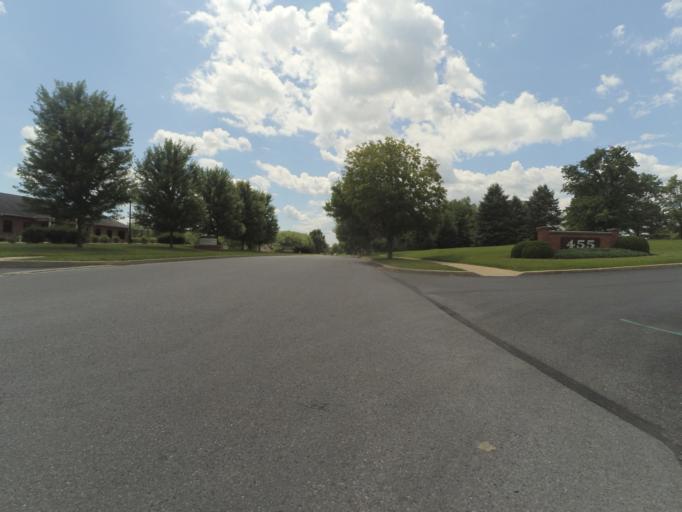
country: US
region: Pennsylvania
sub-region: Centre County
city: Lemont
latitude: 40.7884
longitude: -77.8245
